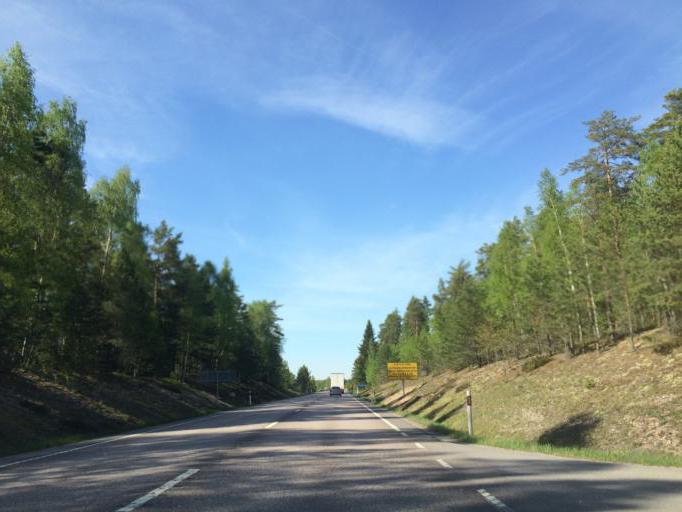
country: SE
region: Vaestmanland
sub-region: Kungsors Kommun
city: Kungsoer
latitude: 59.2319
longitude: 16.1025
